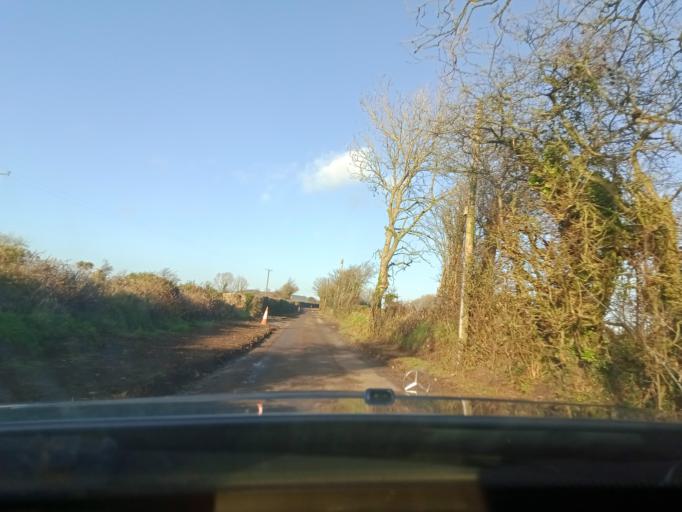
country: IE
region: Munster
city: Carrick-on-Suir
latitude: 52.4446
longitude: -7.3927
